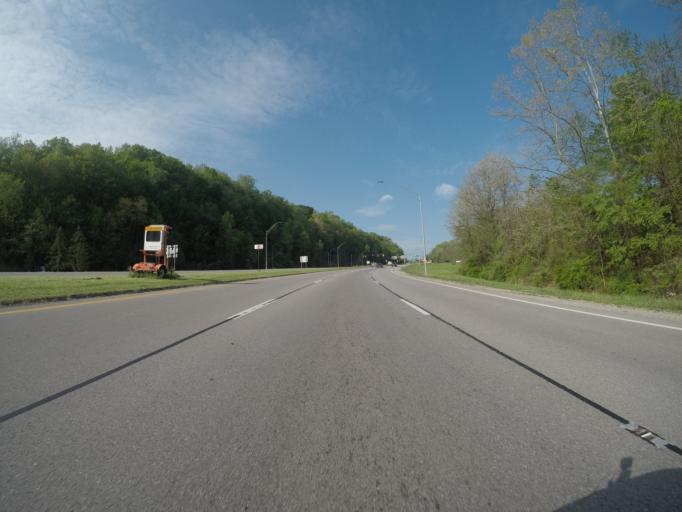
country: US
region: West Virginia
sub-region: Kanawha County
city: Charleston
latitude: 38.3474
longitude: -81.6517
